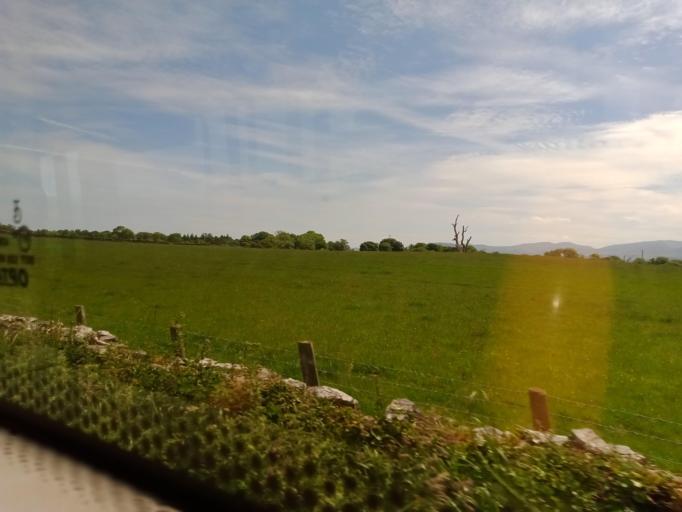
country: GB
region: Wales
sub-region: Anglesey
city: Beaumaris
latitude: 53.2607
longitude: -4.1188
